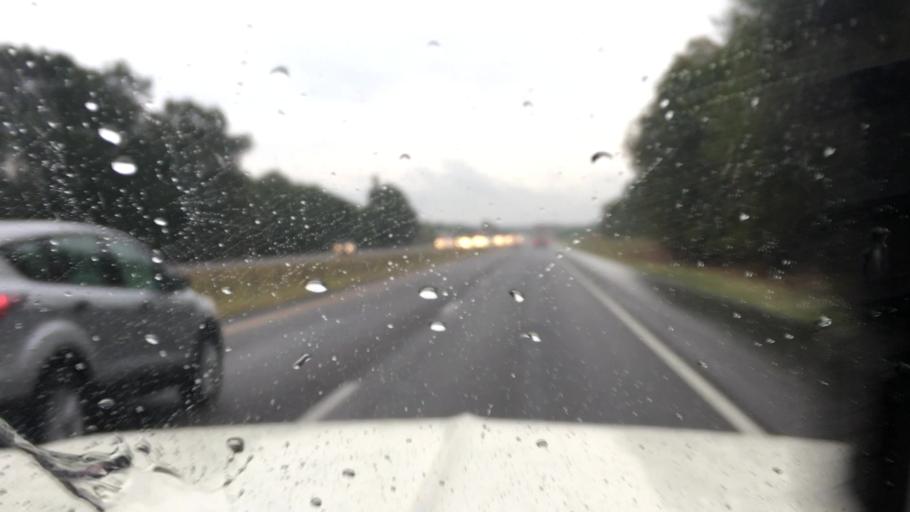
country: US
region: Alabama
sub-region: Morgan County
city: Hartselle
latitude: 34.4201
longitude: -86.8989
